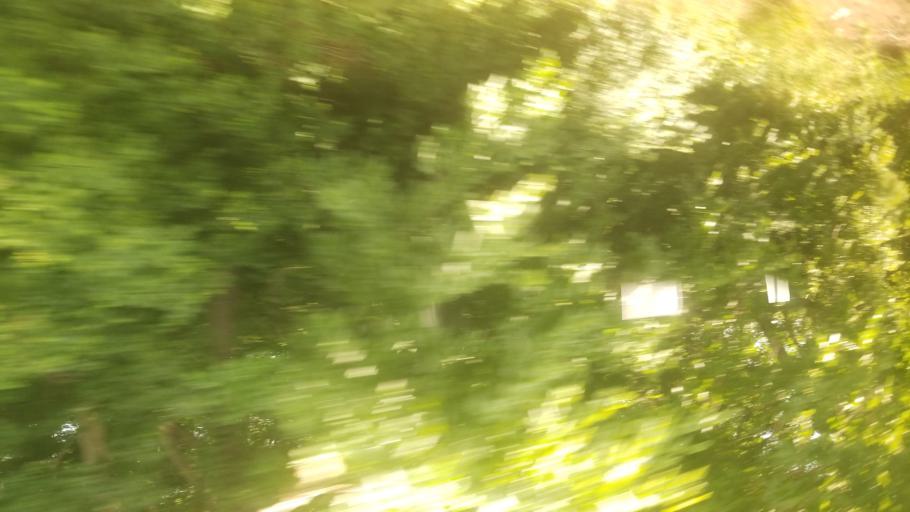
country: US
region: Kansas
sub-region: Wyandotte County
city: Edwardsville
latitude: 39.0445
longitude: -94.8176
